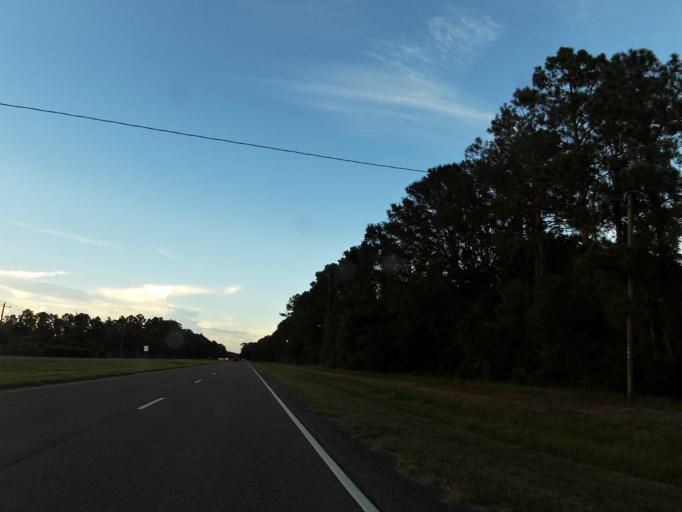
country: US
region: Georgia
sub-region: Camden County
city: Kings Bay Base
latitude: 30.7844
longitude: -81.5767
